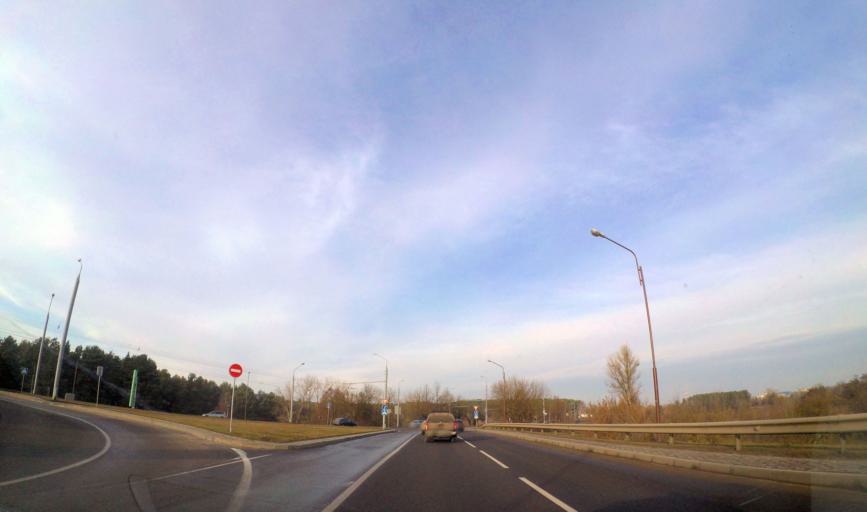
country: BY
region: Grodnenskaya
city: Hrodna
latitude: 53.6763
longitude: 23.8058
